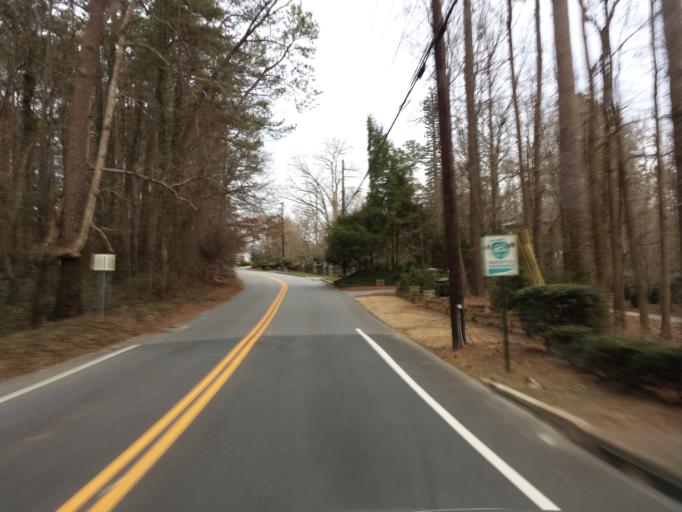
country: US
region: Georgia
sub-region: Cobb County
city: Vinings
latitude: 33.8784
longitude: -84.4138
